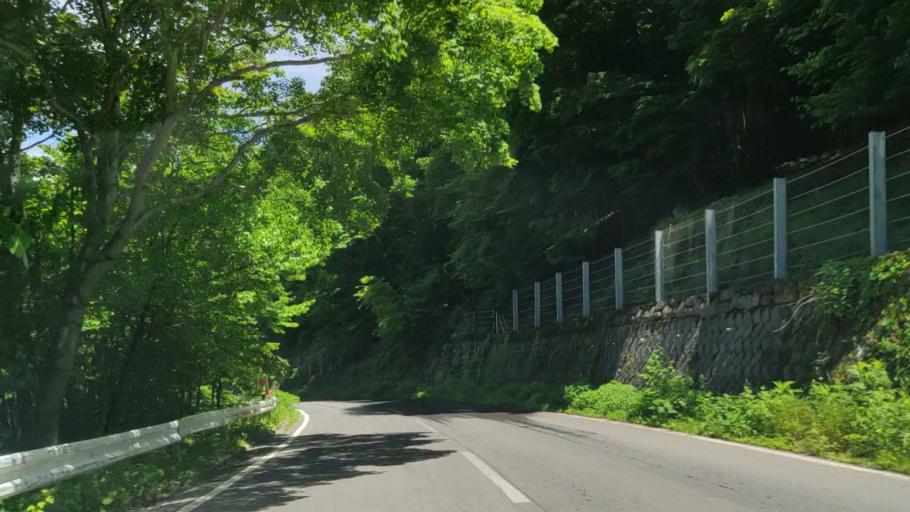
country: JP
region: Nagano
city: Kamimaruko
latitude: 36.1557
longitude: 138.2398
